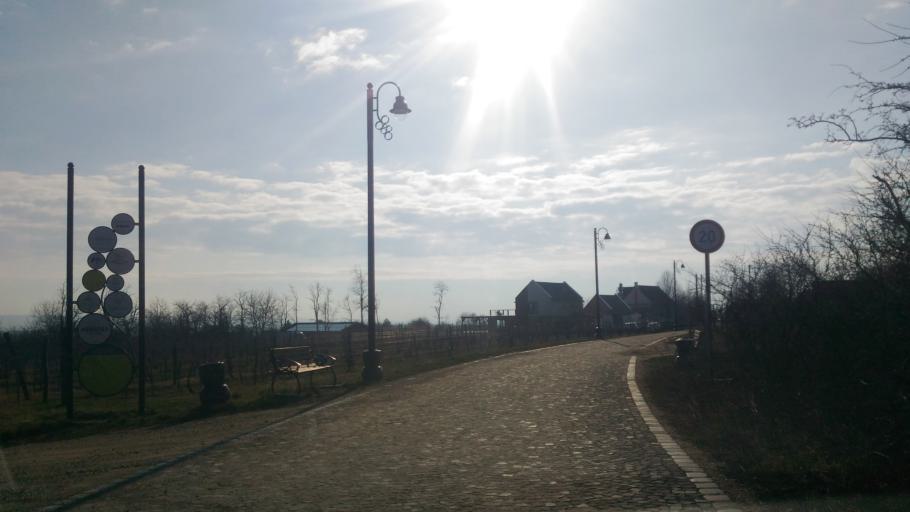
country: HU
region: Fejer
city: Etyek
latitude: 47.4425
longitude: 18.7375
